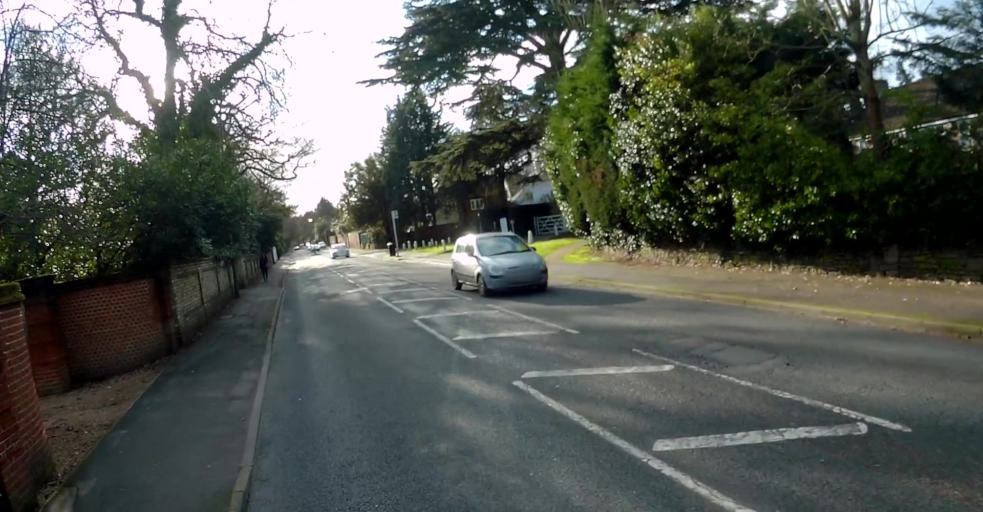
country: GB
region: England
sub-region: Surrey
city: Weybridge
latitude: 51.3668
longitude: -0.4534
